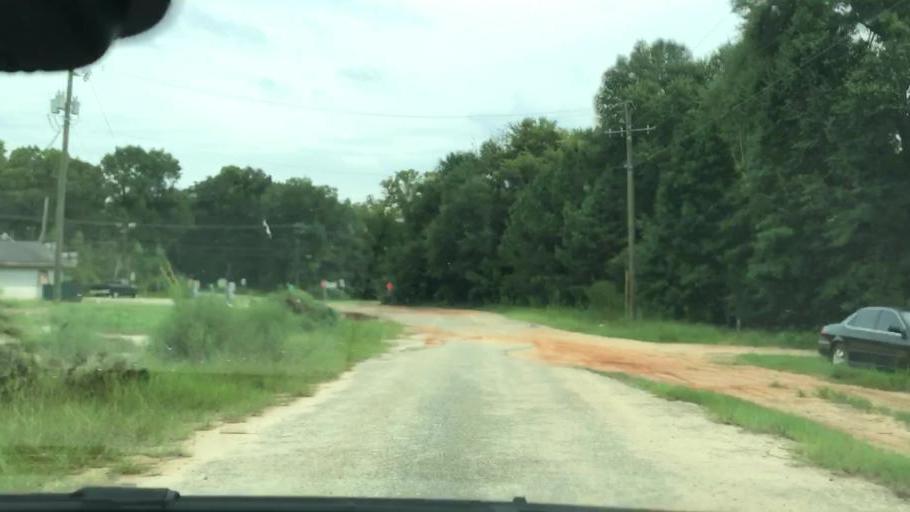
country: US
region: Georgia
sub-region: Clay County
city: Fort Gaines
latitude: 31.6271
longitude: -85.0481
